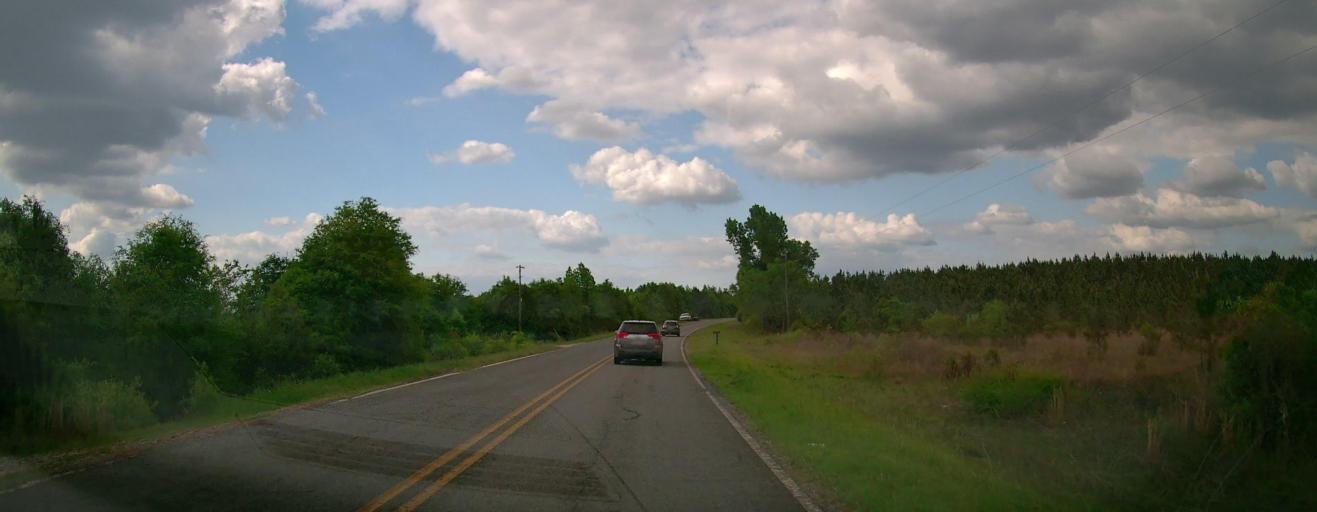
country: US
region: Georgia
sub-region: Washington County
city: Tennille
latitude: 32.7633
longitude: -82.9305
